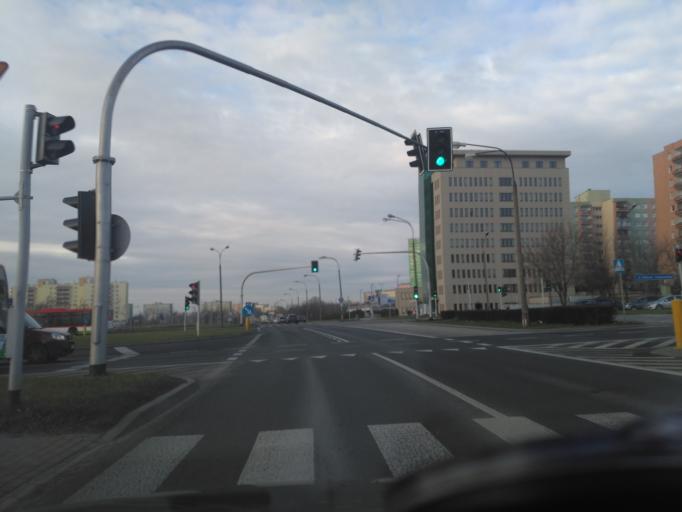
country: PL
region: Lublin Voivodeship
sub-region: Powiat lubelski
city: Lublin
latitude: 51.2634
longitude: 22.5590
